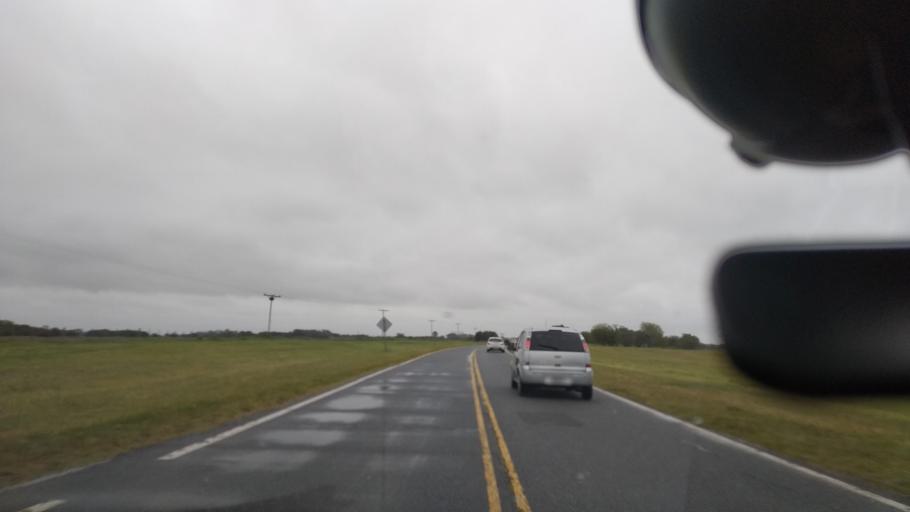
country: AR
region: Buenos Aires
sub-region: Partido de Castelli
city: Castelli
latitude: -35.9703
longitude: -57.4495
